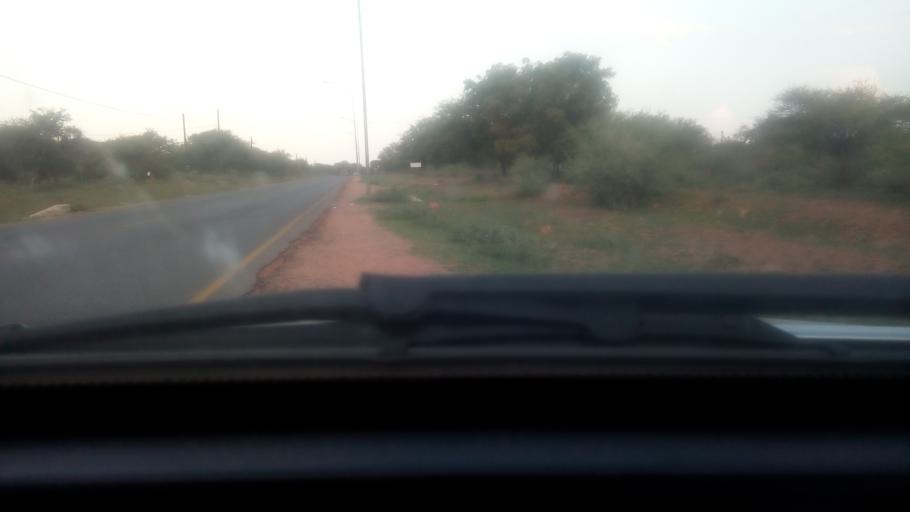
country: BW
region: Kgatleng
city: Bokaa
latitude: -24.4349
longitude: 26.0397
